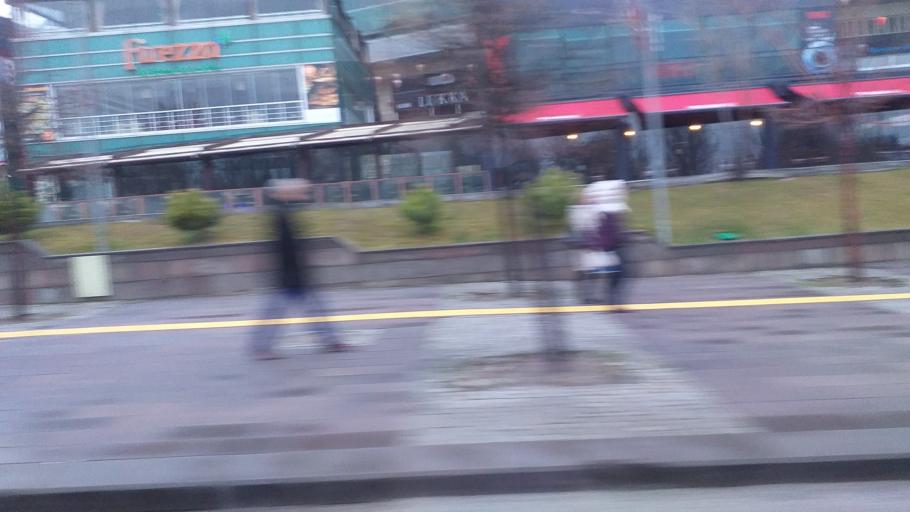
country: TR
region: Ankara
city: Ankara
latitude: 39.9690
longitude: 32.8202
